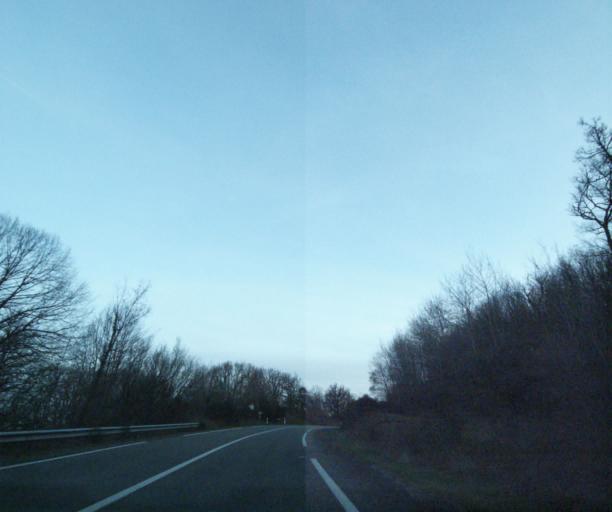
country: FR
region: Midi-Pyrenees
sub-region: Departement du Lot
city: Pradines
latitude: 44.5779
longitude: 1.4724
